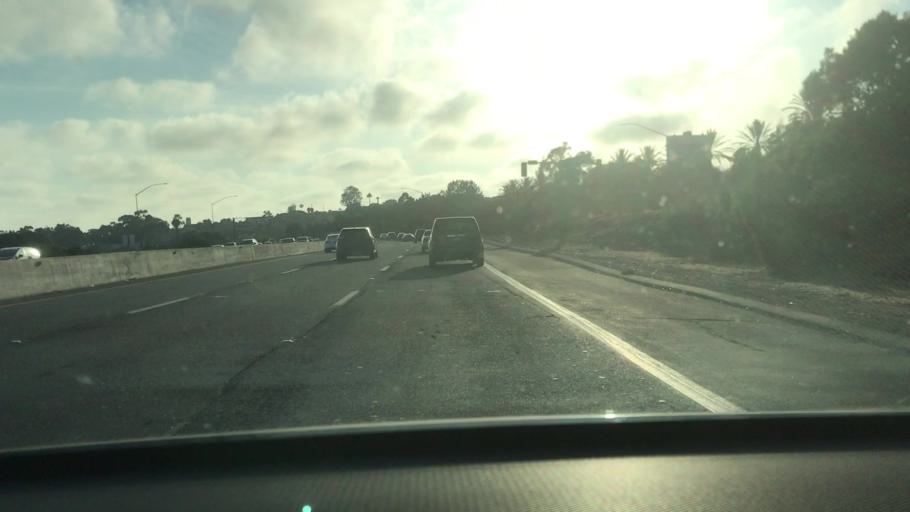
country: US
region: California
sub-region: San Diego County
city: Carlsbad
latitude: 33.1813
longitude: -117.3406
